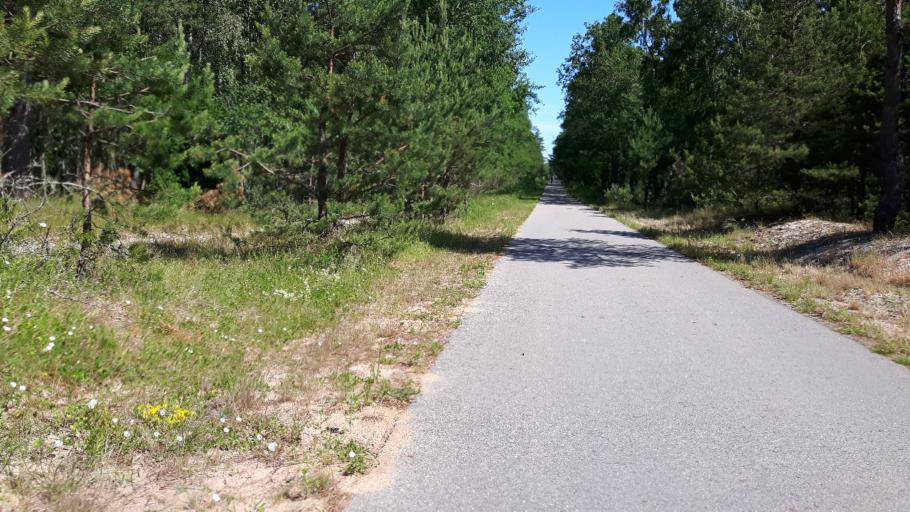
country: LT
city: Neringa
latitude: 55.3387
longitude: 21.0377
